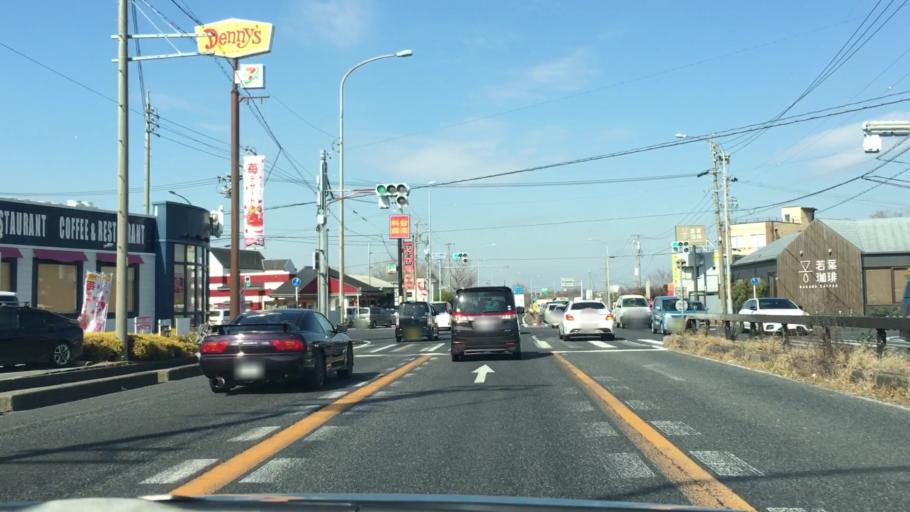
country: JP
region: Aichi
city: Okazaki
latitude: 34.9299
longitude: 137.1977
